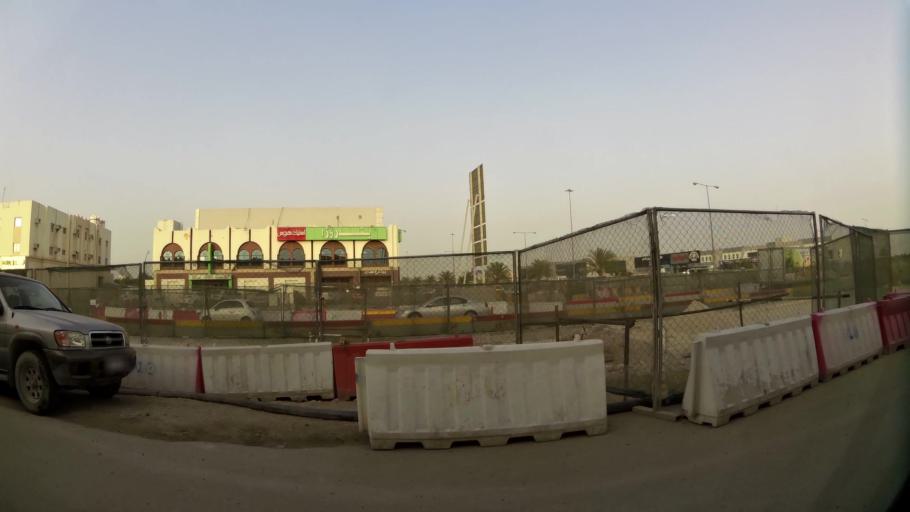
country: QA
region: Baladiyat ar Rayyan
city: Ar Rayyan
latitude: 25.2407
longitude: 51.4560
